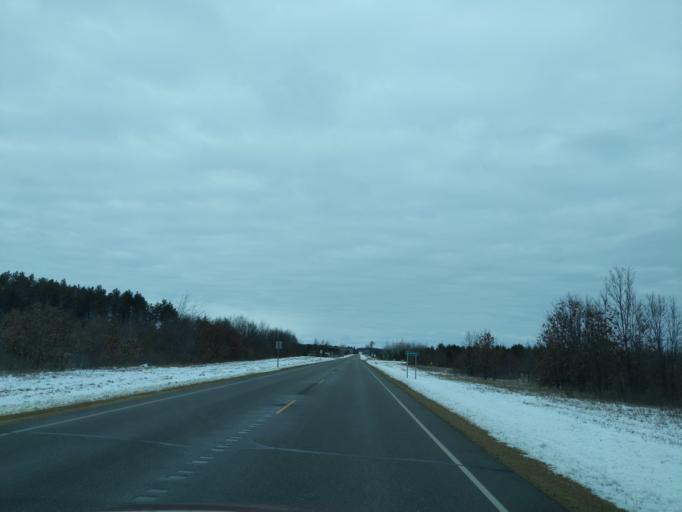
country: US
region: Wisconsin
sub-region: Waushara County
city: Wautoma
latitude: 43.9803
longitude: -89.3276
